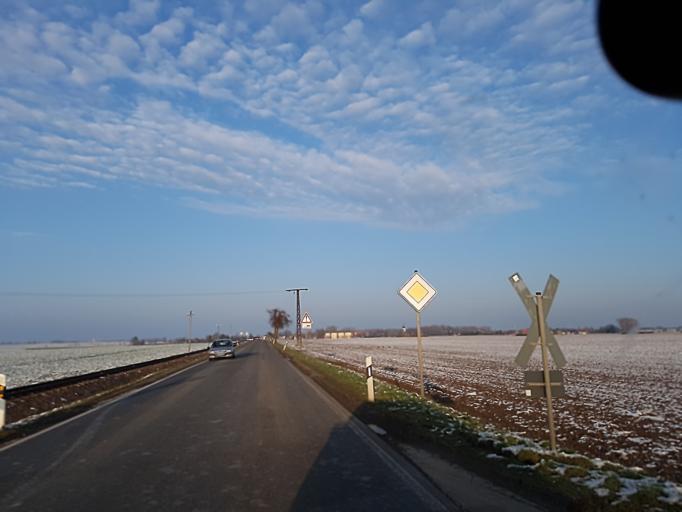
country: DE
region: Saxony
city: Naundorf
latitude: 51.2511
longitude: 13.0918
